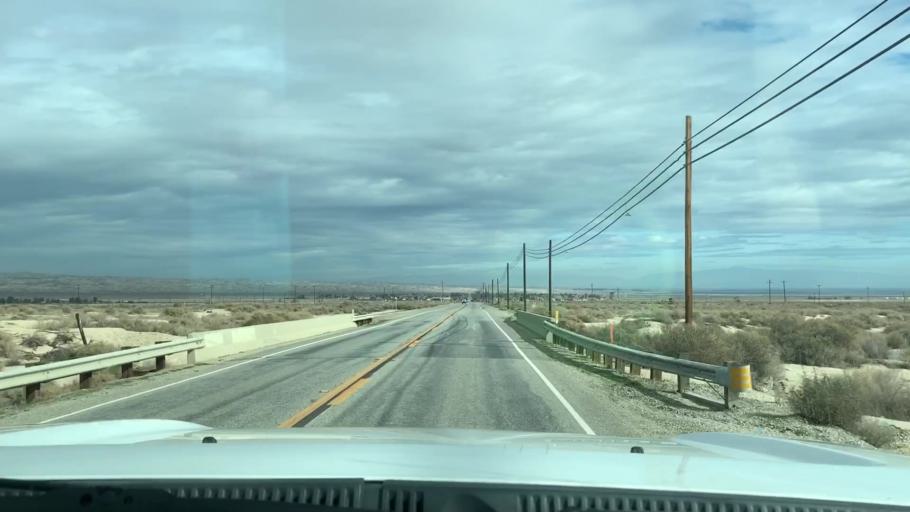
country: US
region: California
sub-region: Kern County
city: Ford City
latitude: 35.1910
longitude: -119.4329
